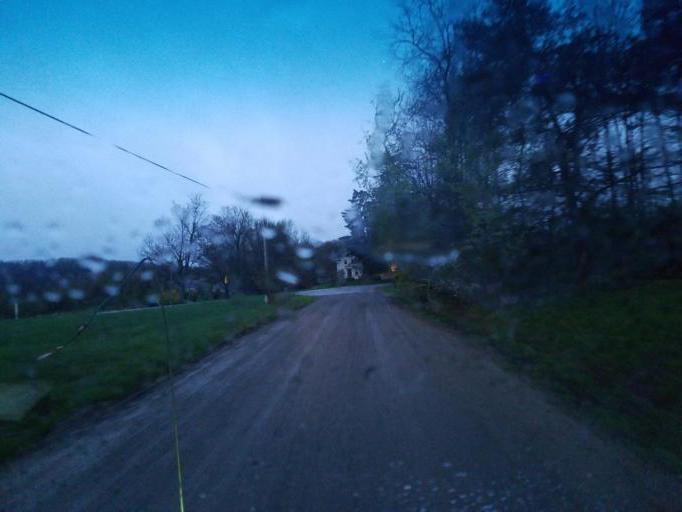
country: US
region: Pennsylvania
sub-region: Tioga County
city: Westfield
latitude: 41.9264
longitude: -77.7309
